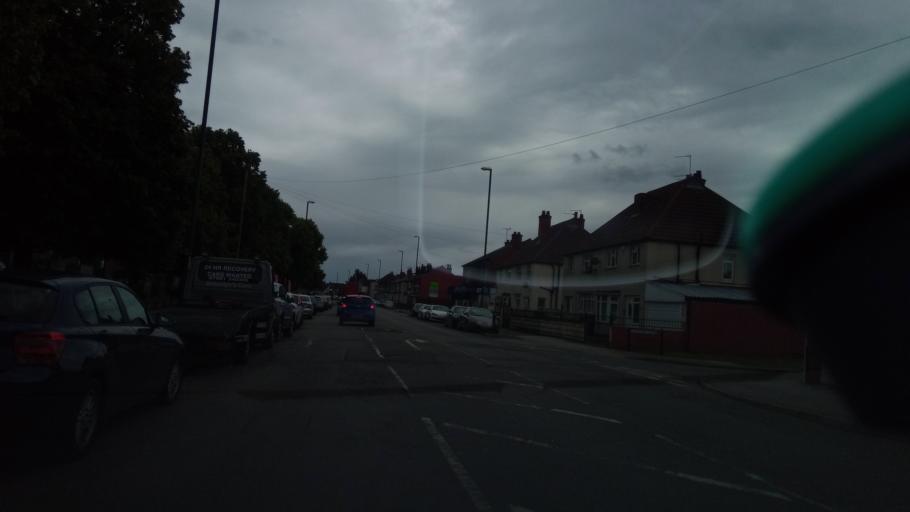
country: GB
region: England
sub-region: Derby
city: Derby
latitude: 52.8988
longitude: -1.4577
